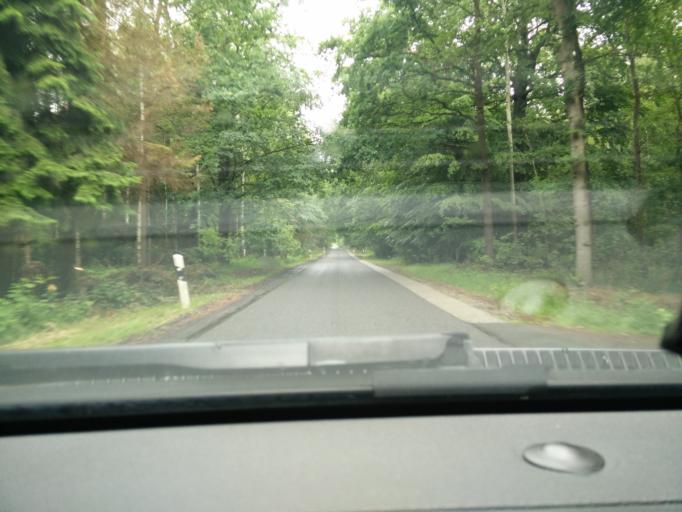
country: DE
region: Saxony
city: Bad Lausick
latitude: 51.1203
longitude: 12.6854
